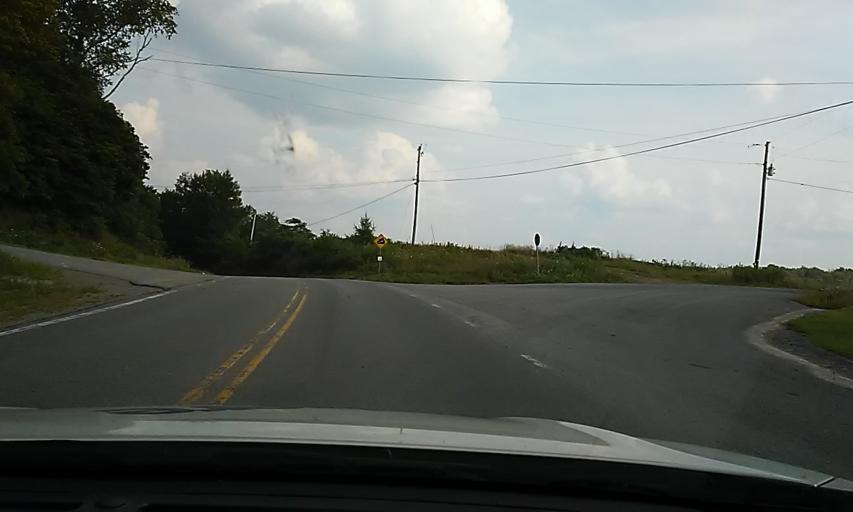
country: US
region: Pennsylvania
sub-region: Potter County
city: Coudersport
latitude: 41.8592
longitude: -77.8257
